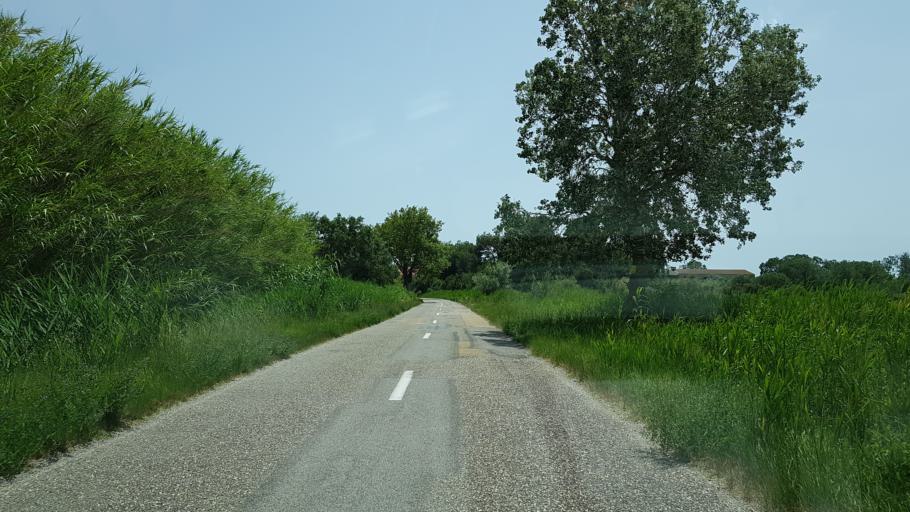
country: FR
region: Provence-Alpes-Cote d'Azur
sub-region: Departement des Bouches-du-Rhone
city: Port-Saint-Louis-du-Rhone
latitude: 43.4524
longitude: 4.6594
